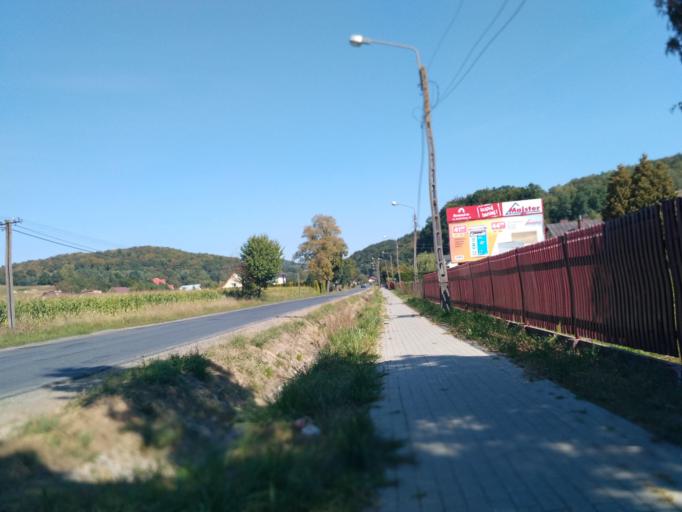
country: PL
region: Subcarpathian Voivodeship
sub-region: Powiat brzozowski
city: Grabownica Starzenska
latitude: 49.6613
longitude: 22.0799
